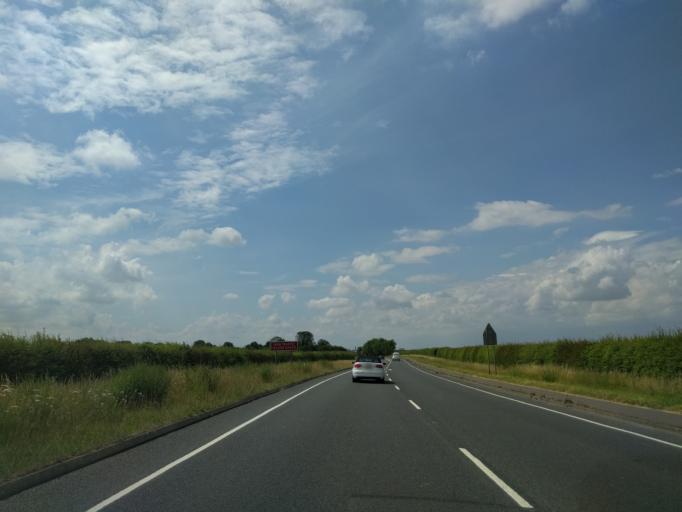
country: GB
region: England
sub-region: Cambridgeshire
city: Fulbourn
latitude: 52.2095
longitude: 0.1901
